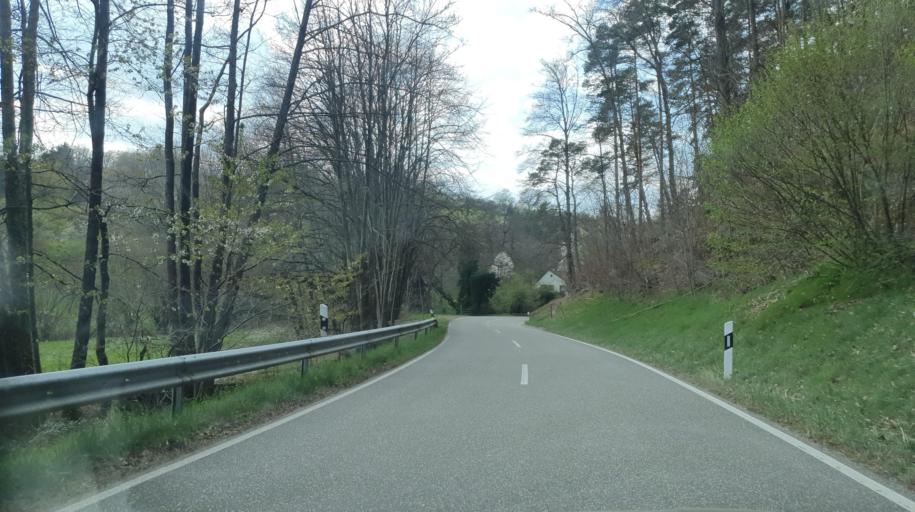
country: DE
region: Rheinland-Pfalz
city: Waldfischbach-Burgalben
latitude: 49.2749
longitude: 7.6616
